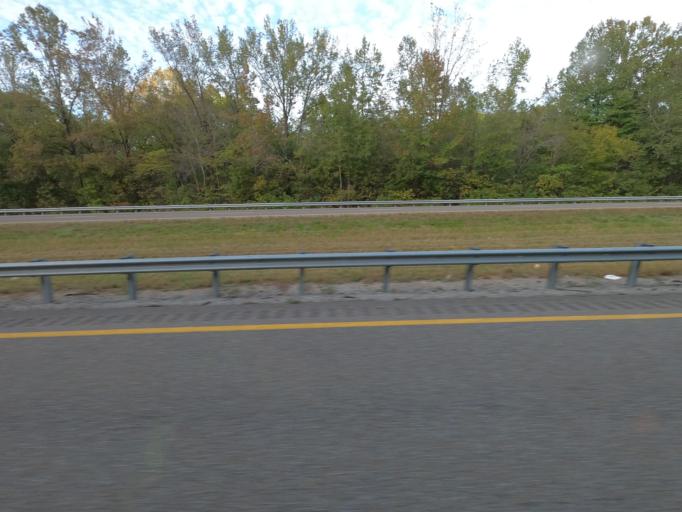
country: US
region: Tennessee
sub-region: Humphreys County
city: New Johnsonville
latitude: 35.8648
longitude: -87.9142
